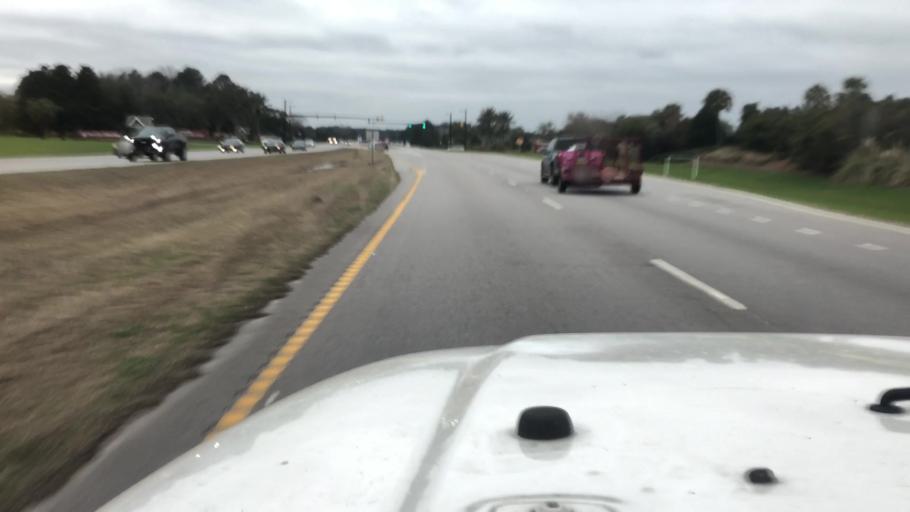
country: US
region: South Carolina
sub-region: Beaufort County
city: Bluffton
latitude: 32.3006
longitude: -80.9539
